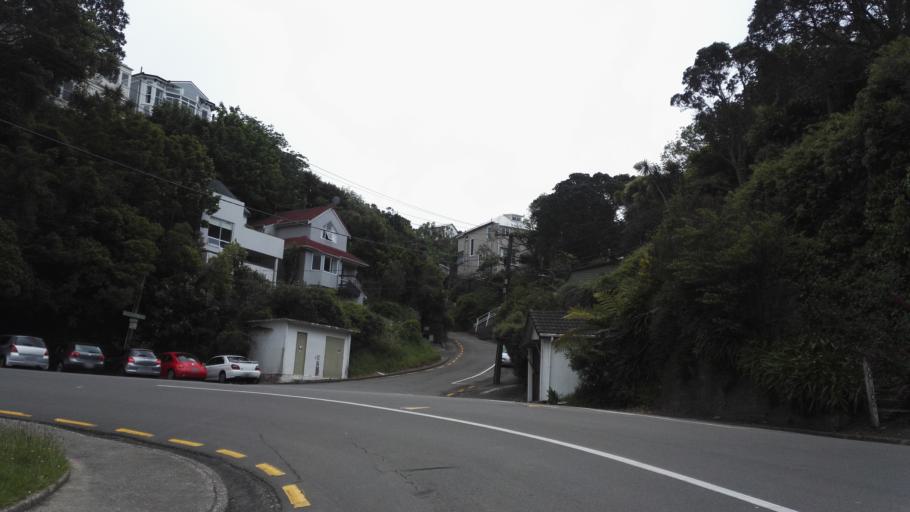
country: NZ
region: Wellington
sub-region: Wellington City
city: Kelburn
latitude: -41.2915
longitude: 174.7656
